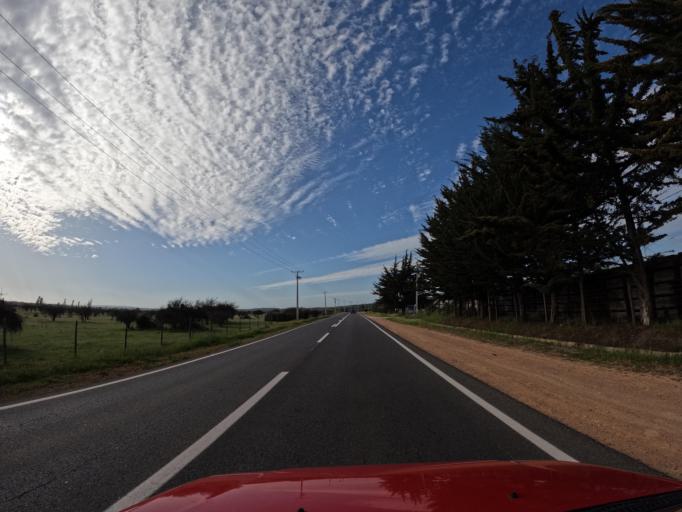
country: CL
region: Valparaiso
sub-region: San Antonio Province
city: San Antonio
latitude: -34.1541
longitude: -71.7329
